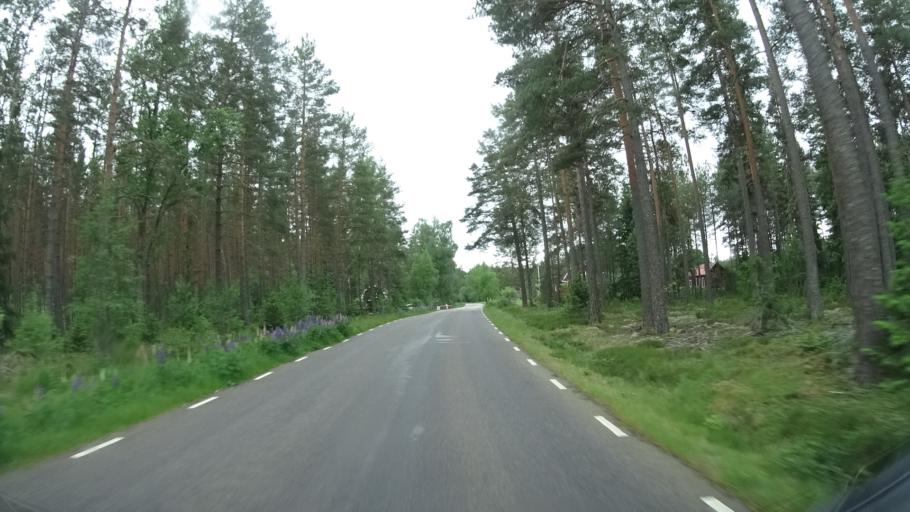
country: SE
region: Joenkoeping
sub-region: Eksjo Kommun
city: Mariannelund
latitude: 57.6969
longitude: 15.6250
